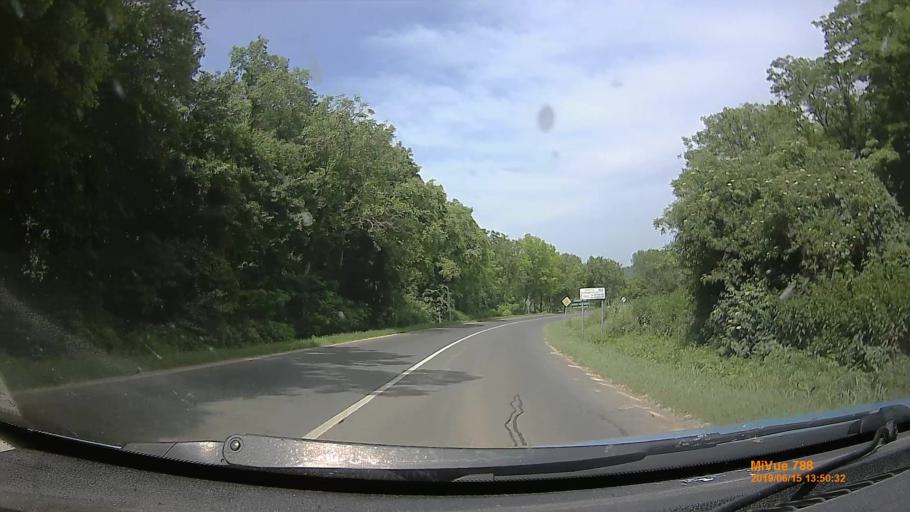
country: HU
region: Tolna
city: Iregszemcse
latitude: 46.7439
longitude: 18.1612
